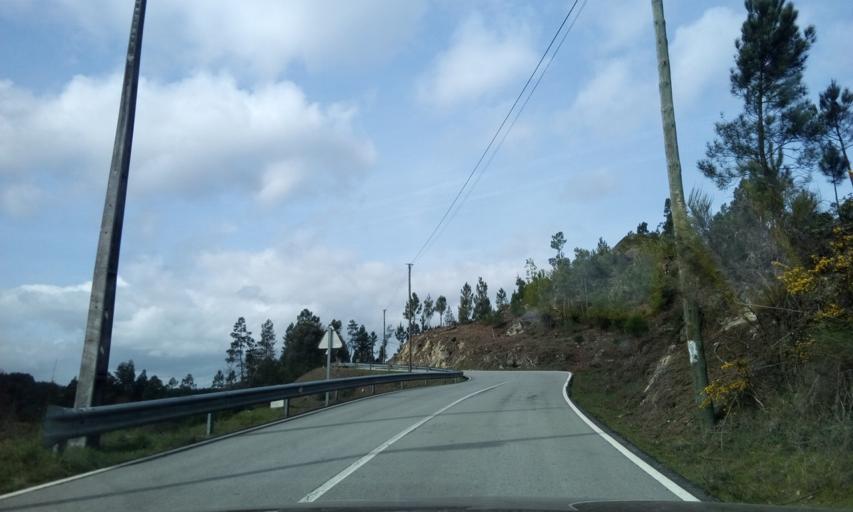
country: PT
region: Viseu
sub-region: Satao
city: Satao
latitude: 40.6663
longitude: -7.6821
